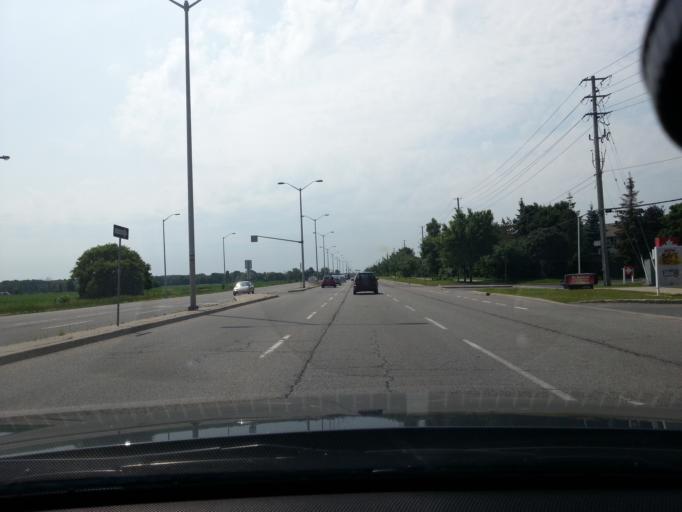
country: CA
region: Ontario
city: Bells Corners
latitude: 45.2983
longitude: -75.7312
